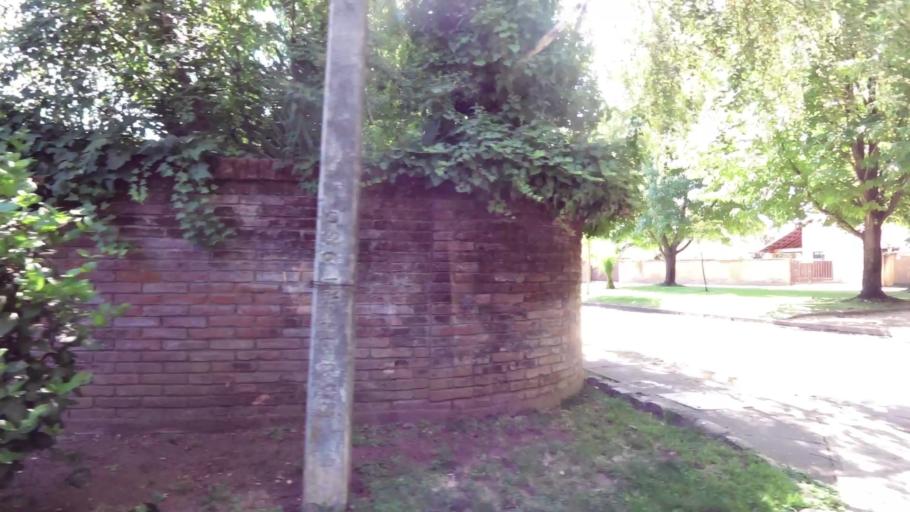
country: CL
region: Maule
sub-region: Provincia de Talca
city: Talca
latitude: -35.4326
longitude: -71.6191
